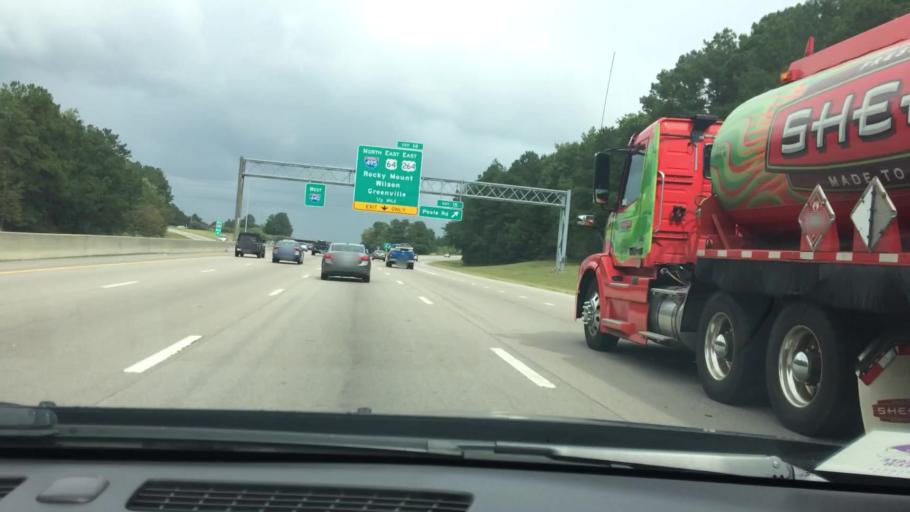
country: US
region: North Carolina
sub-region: Wake County
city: Raleigh
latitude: 35.7634
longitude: -78.5743
